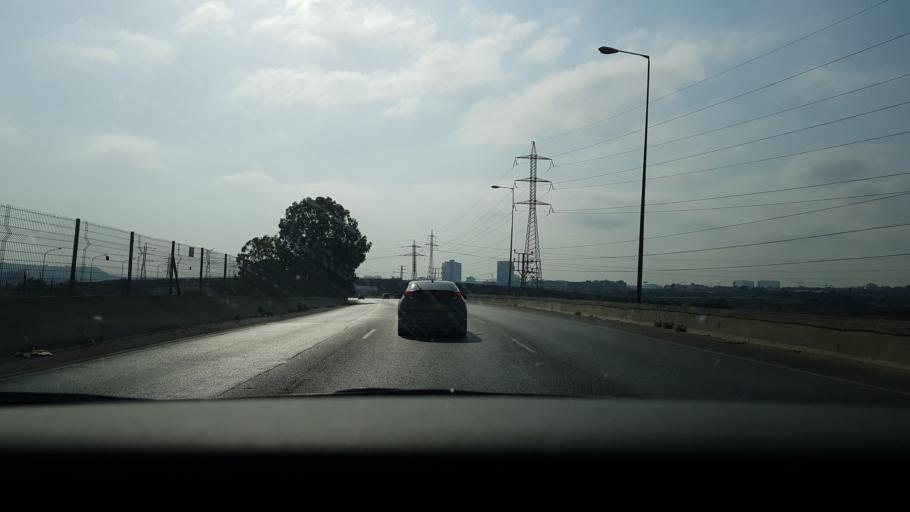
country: IL
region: Tel Aviv
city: Azor
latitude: 32.0407
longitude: 34.7899
